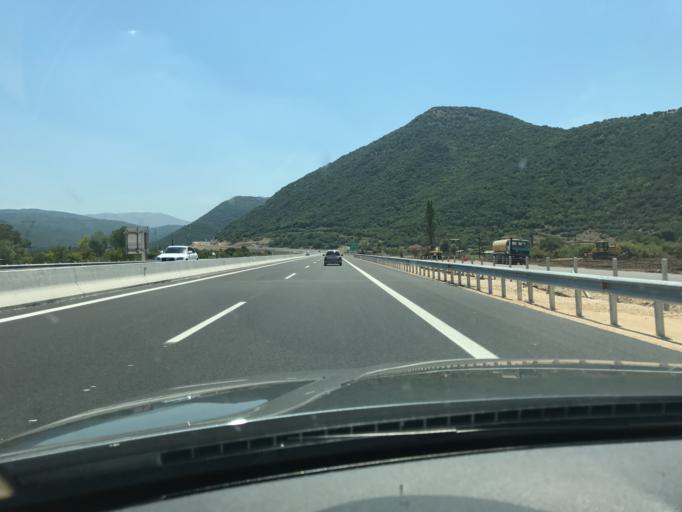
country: GR
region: Epirus
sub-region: Nomos Ioanninon
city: Agia Kyriaki
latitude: 39.5248
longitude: 20.8795
